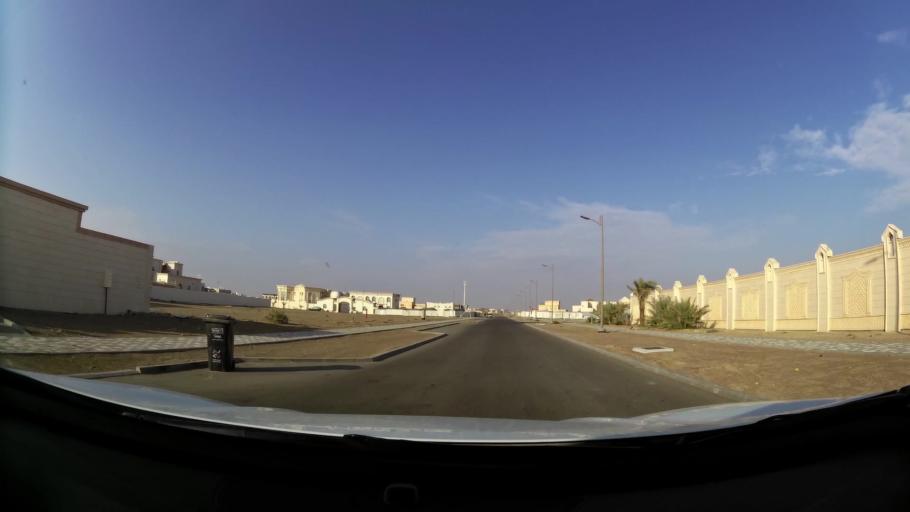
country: AE
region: Abu Dhabi
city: Al Ain
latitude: 24.1059
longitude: 55.8527
